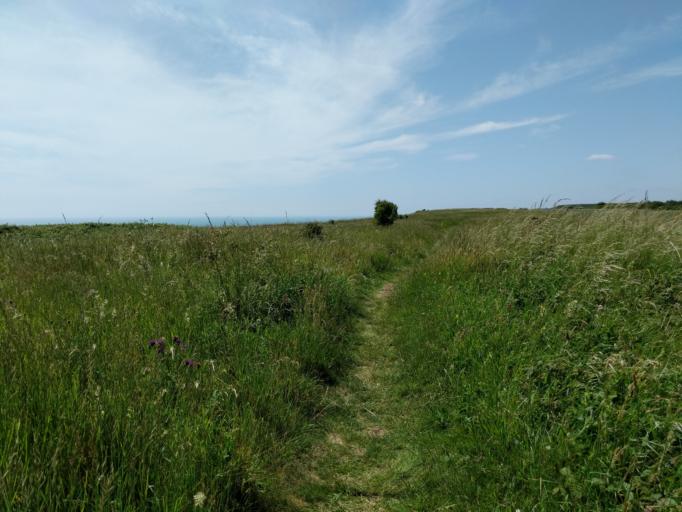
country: GB
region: England
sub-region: Kent
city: Dover
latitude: 51.1048
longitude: 1.2631
